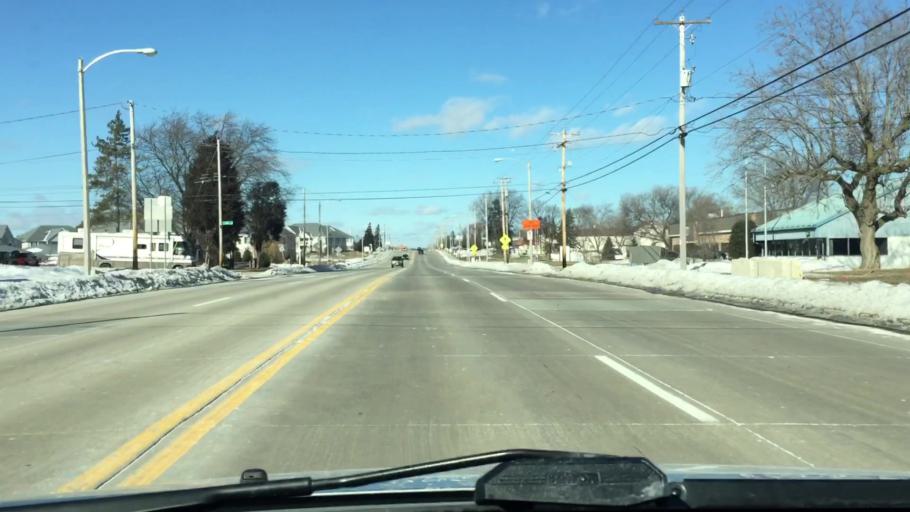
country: US
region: Wisconsin
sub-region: Milwaukee County
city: Greendale
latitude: 42.9175
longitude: -87.9307
